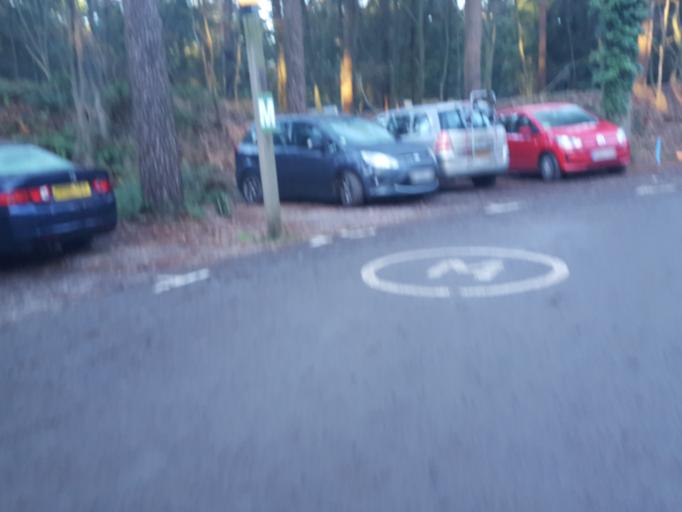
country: GB
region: England
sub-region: Wiltshire
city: Corsley
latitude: 51.1880
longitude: -2.2283
